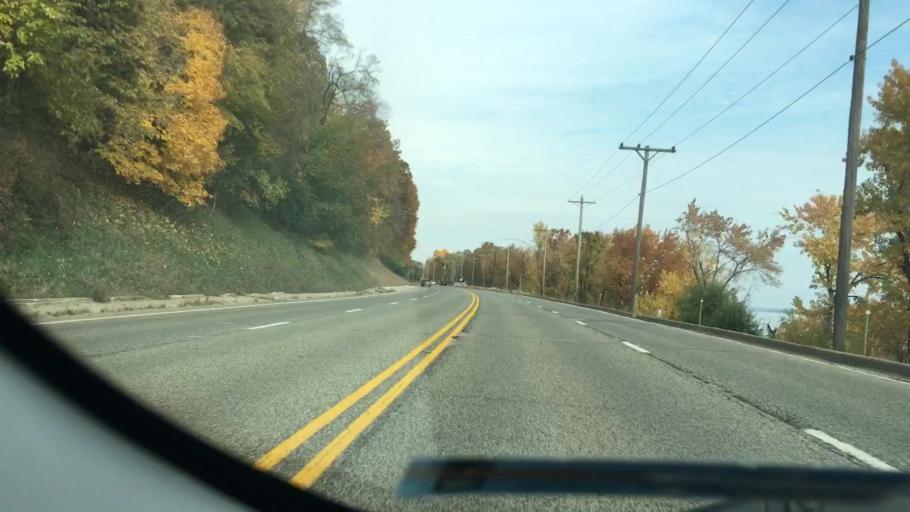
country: US
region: Illinois
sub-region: Peoria County
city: Peoria Heights
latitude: 40.7349
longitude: -89.5516
